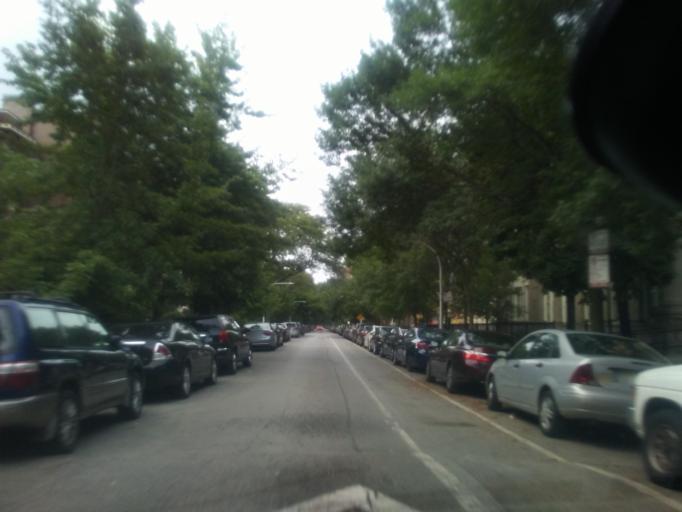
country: US
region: Illinois
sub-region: Cook County
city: Evanston
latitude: 41.9894
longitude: -87.6582
